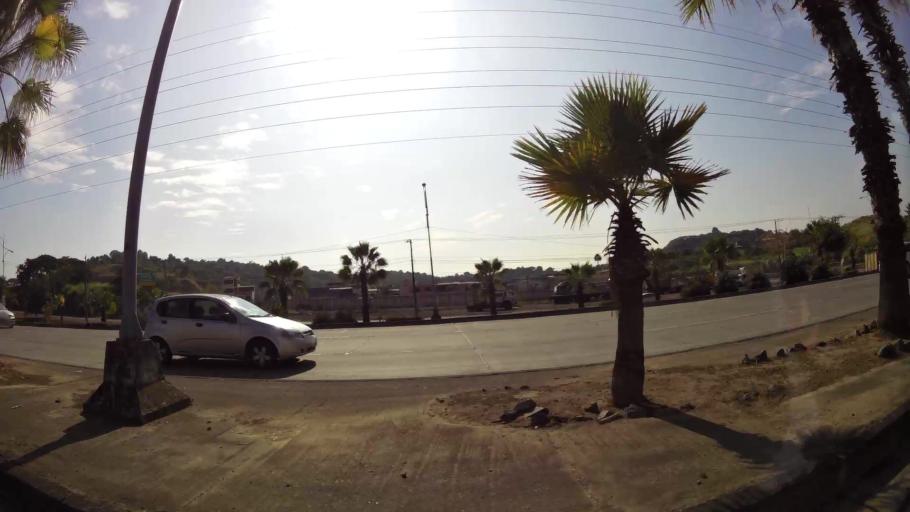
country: EC
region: Guayas
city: Eloy Alfaro
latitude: -2.0787
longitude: -79.9164
